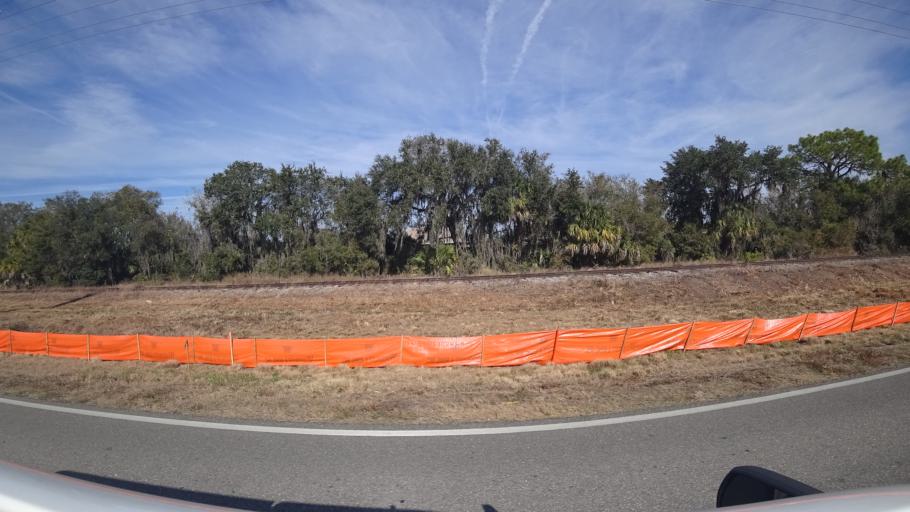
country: US
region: Florida
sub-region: Manatee County
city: Ellenton
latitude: 27.5830
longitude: -82.4442
